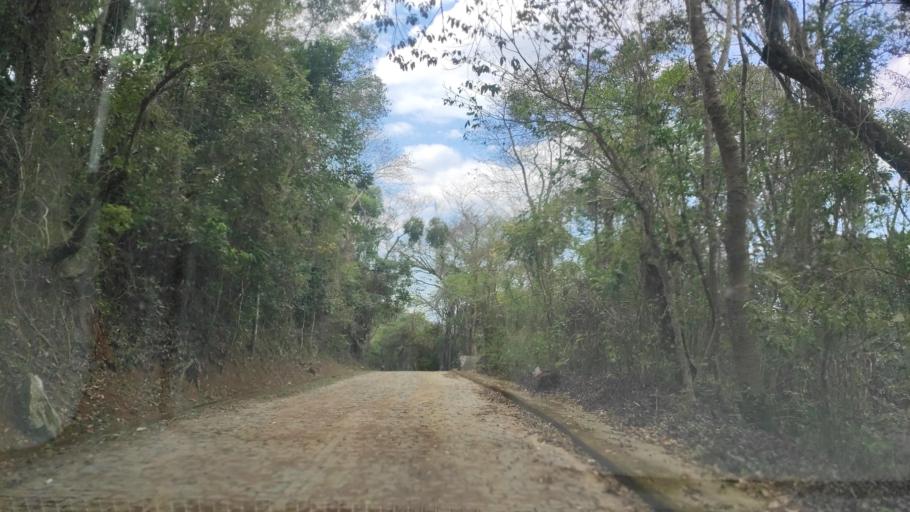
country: BR
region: Espirito Santo
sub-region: Vitoria
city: Vitoria
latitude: -20.3069
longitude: -40.3405
